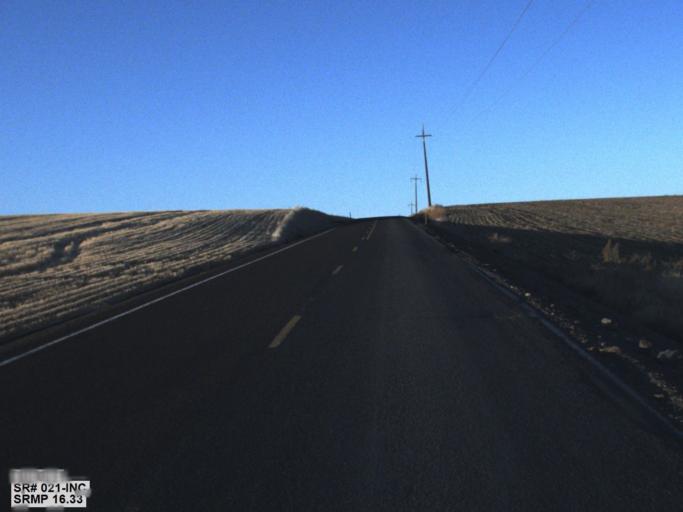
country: US
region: Washington
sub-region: Adams County
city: Ritzville
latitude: 46.8627
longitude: -118.5468
